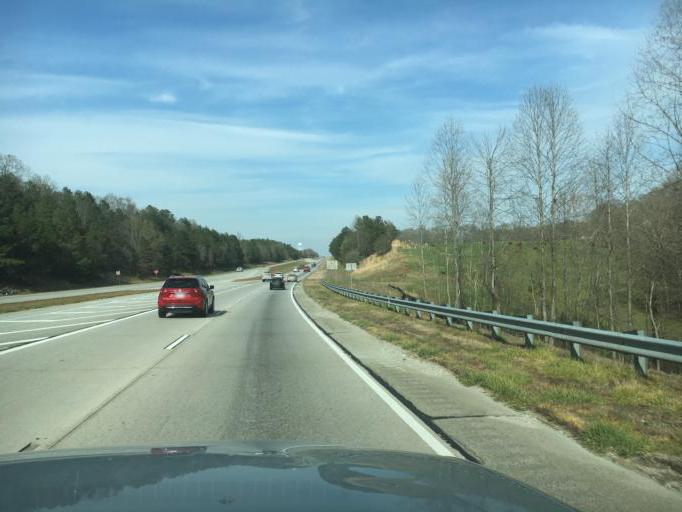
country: US
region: Georgia
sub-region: Hall County
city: Lula
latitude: 34.3855
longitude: -83.7072
